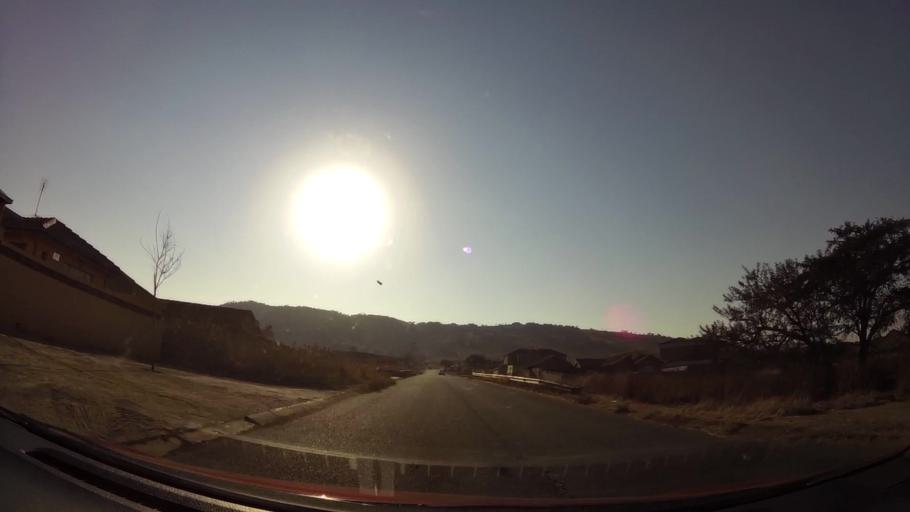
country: ZA
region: Gauteng
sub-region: City of Johannesburg Metropolitan Municipality
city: Soweto
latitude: -26.2943
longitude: 27.9588
